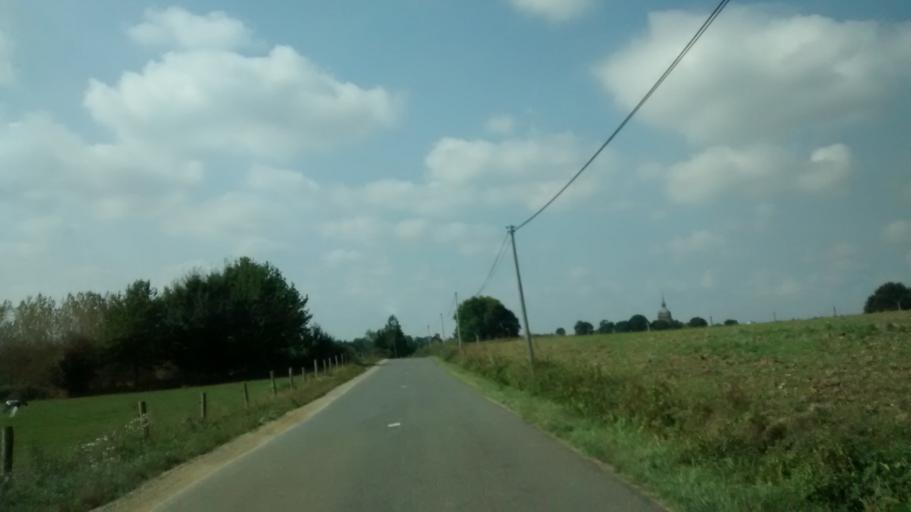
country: FR
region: Brittany
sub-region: Departement d'Ille-et-Vilaine
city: Livre-sur-Changeon
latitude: 48.2185
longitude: -1.3323
